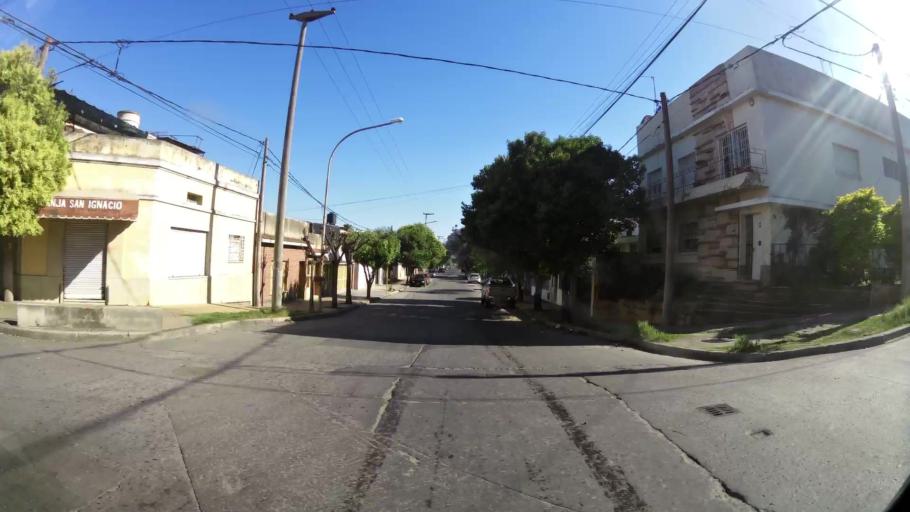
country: AR
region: Cordoba
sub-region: Departamento de Capital
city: Cordoba
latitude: -31.4262
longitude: -64.1409
